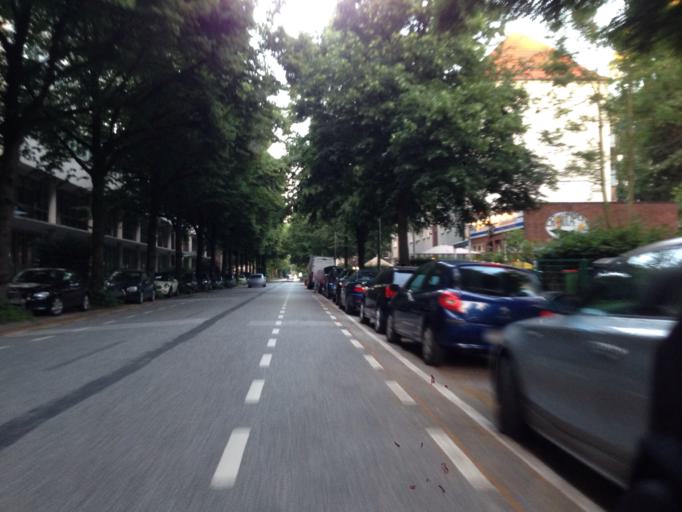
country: DE
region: Hamburg
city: Hamburg
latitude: 53.5811
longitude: 10.0229
